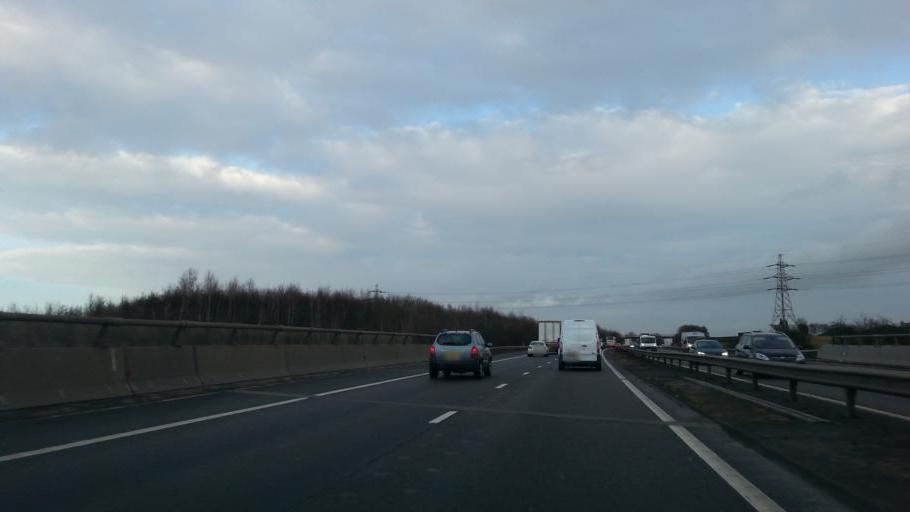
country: GB
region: England
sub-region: Warwickshire
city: Kingsbury
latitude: 52.5789
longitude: -1.6806
